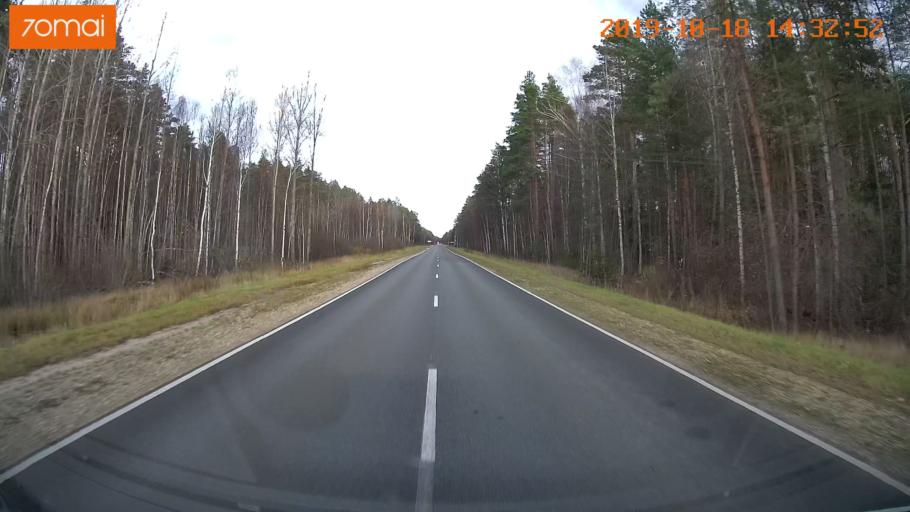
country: RU
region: Rjazan
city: Tuma
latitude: 55.1952
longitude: 40.5865
